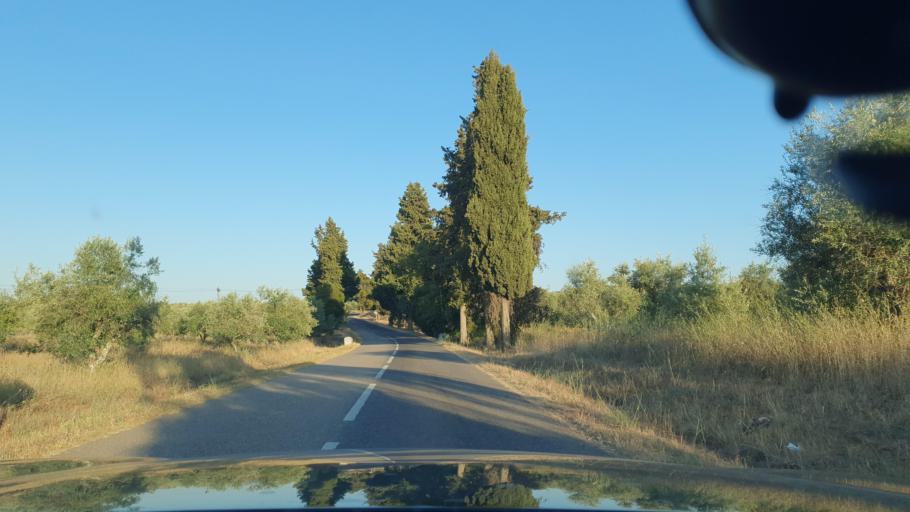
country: PT
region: Portalegre
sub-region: Fronteira
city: Fronteira
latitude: 38.9389
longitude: -7.6746
